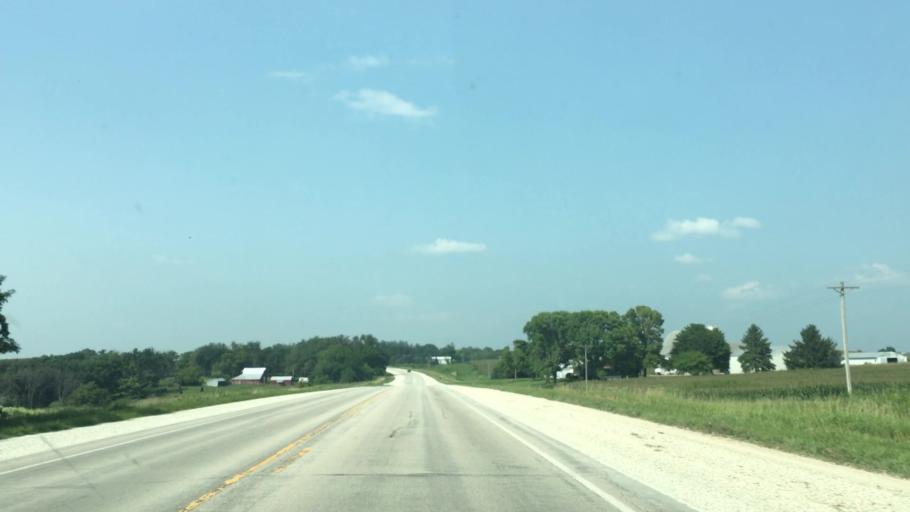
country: US
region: Iowa
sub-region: Winneshiek County
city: Decorah
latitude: 43.4226
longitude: -91.8596
